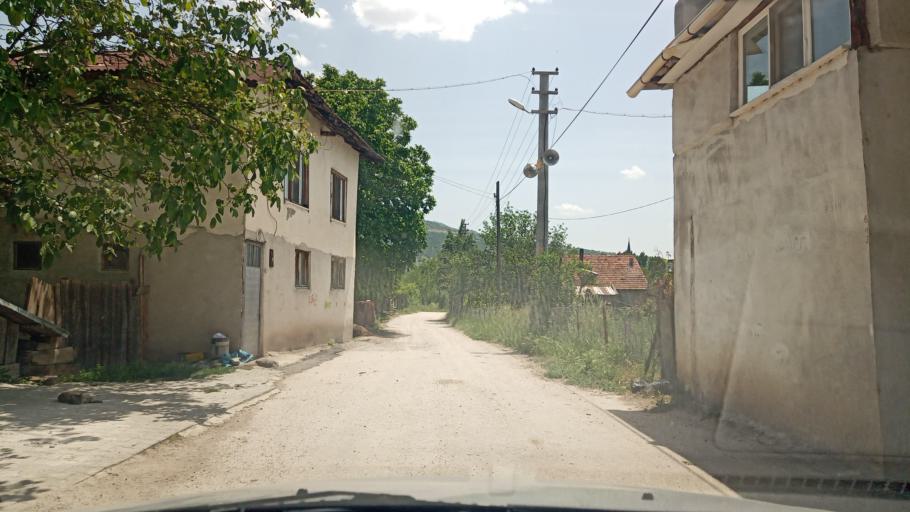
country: TR
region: Bolu
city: Seben
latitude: 40.4127
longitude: 31.5790
